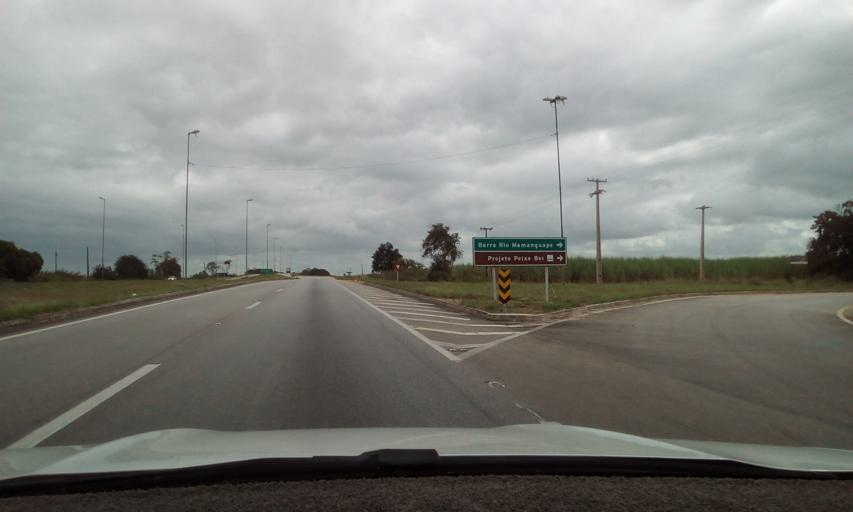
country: BR
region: Paraiba
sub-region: Mamanguape
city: Mamanguape
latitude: -6.9317
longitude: -35.1028
